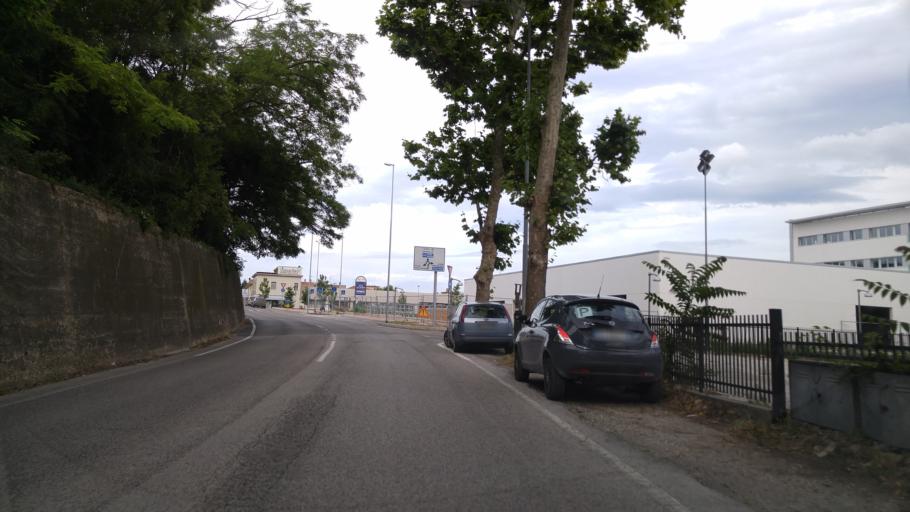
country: IT
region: The Marches
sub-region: Provincia di Pesaro e Urbino
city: Pesaro
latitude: 43.9081
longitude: 12.8673
